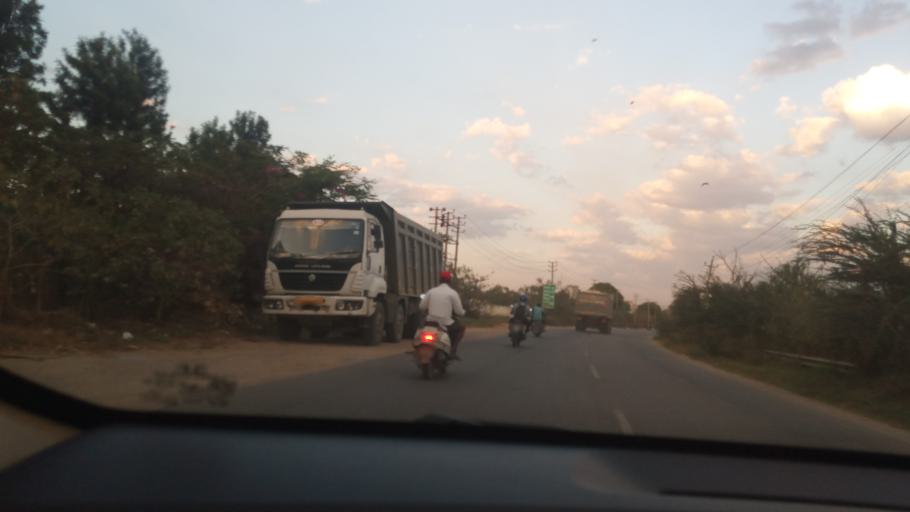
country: IN
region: Karnataka
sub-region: Bangalore Rural
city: Hoskote
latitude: 12.9794
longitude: 77.7954
